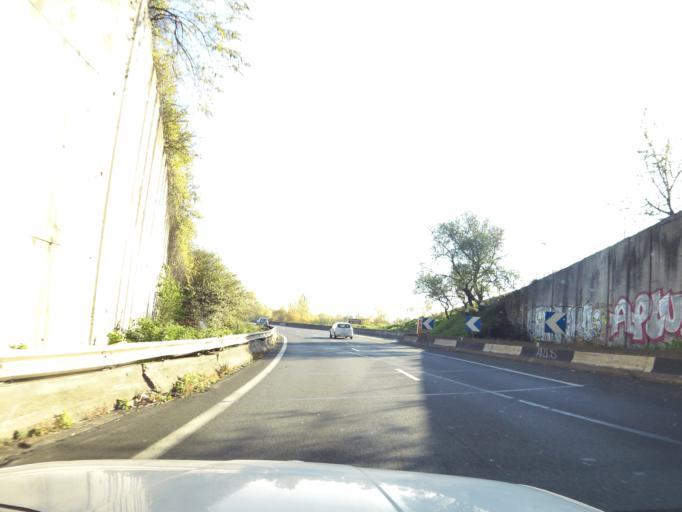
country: FR
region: Rhone-Alpes
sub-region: Departement du Rhone
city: Vaulx-en-Velin
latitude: 45.8053
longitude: 4.9247
